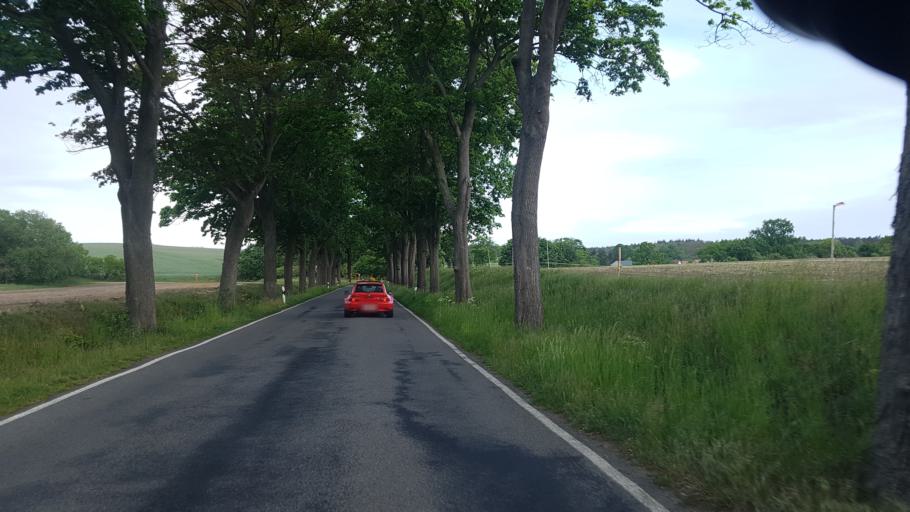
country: DE
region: Brandenburg
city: Baruth
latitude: 52.0052
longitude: 13.4727
